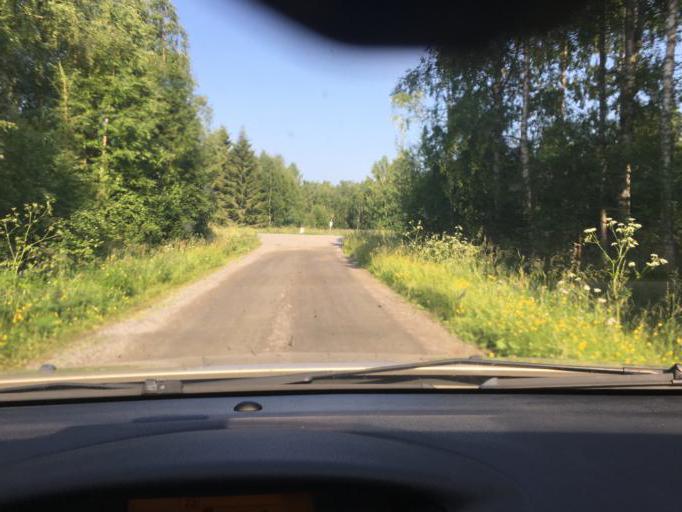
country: SE
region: Norrbotten
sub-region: Kalix Kommun
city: Toere
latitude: 65.8565
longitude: 22.6758
